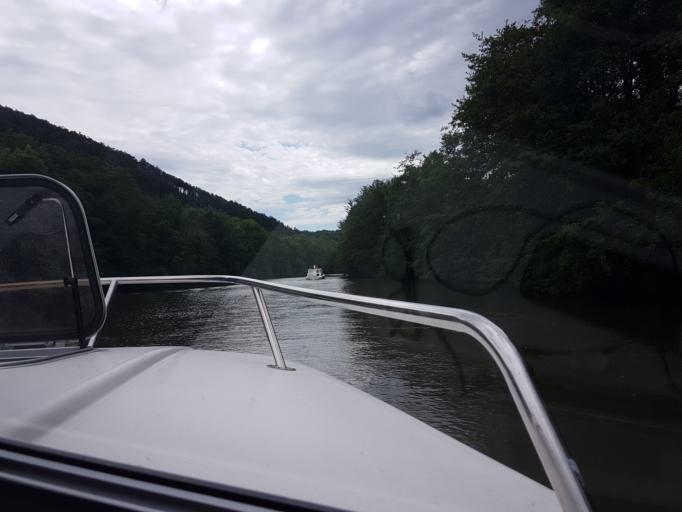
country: FR
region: Bourgogne
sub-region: Departement de la Nievre
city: Clamecy
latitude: 47.4739
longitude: 3.5270
